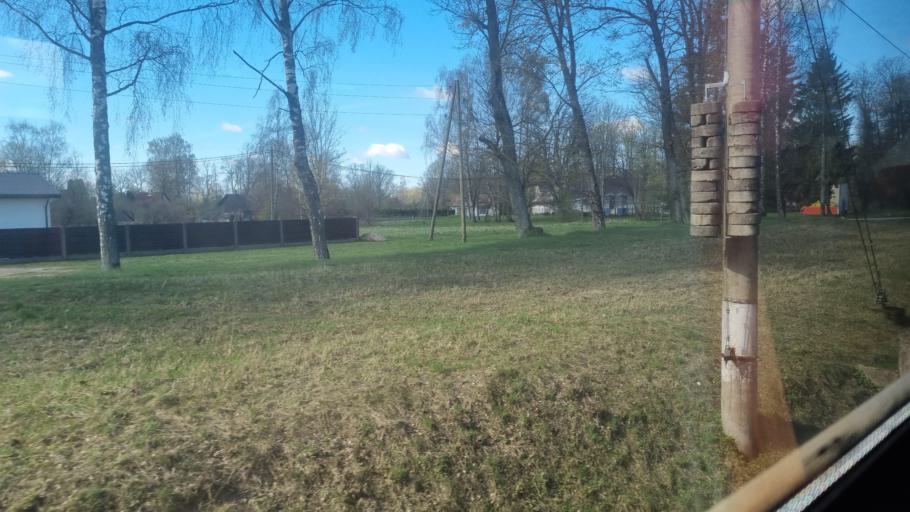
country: LV
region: Lielvarde
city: Lielvarde
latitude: 56.7216
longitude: 24.8118
